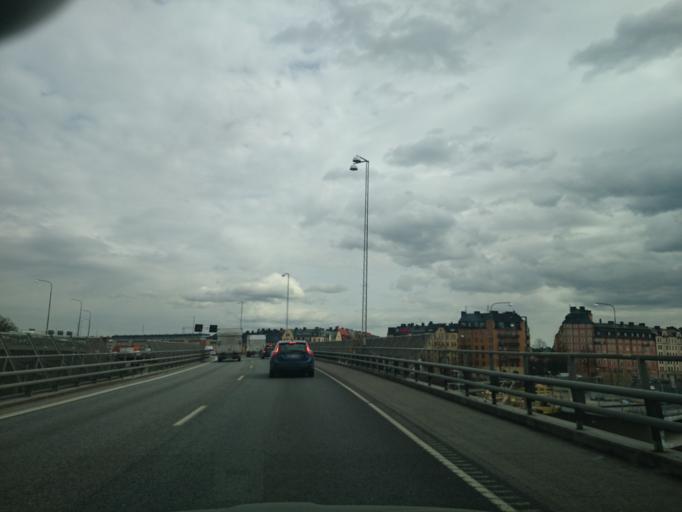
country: SE
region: Stockholm
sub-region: Solna Kommun
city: Solna
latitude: 59.3438
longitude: 18.0222
